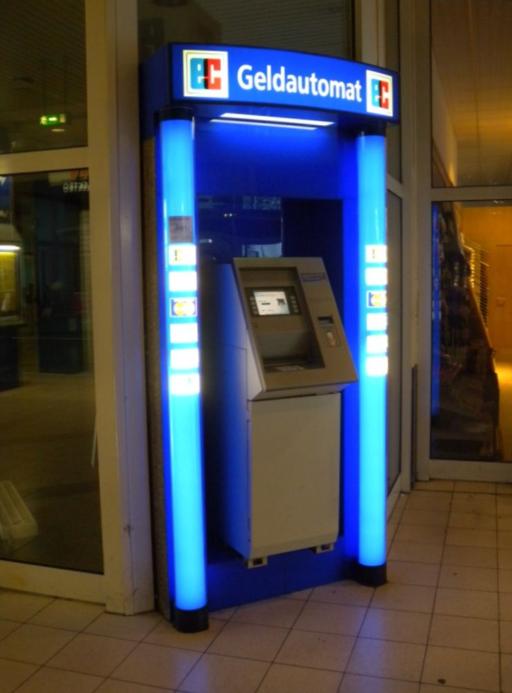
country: DE
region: Baden-Wuerttemberg
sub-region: Regierungsbezirk Stuttgart
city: Ludwigsburg
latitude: 48.8925
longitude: 9.1857
